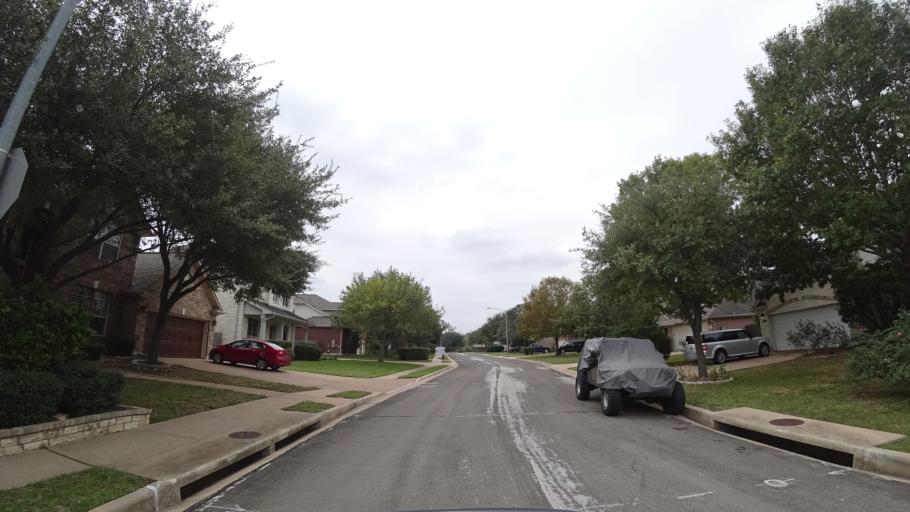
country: US
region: Texas
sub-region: Travis County
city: Shady Hollow
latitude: 30.2088
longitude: -97.8841
